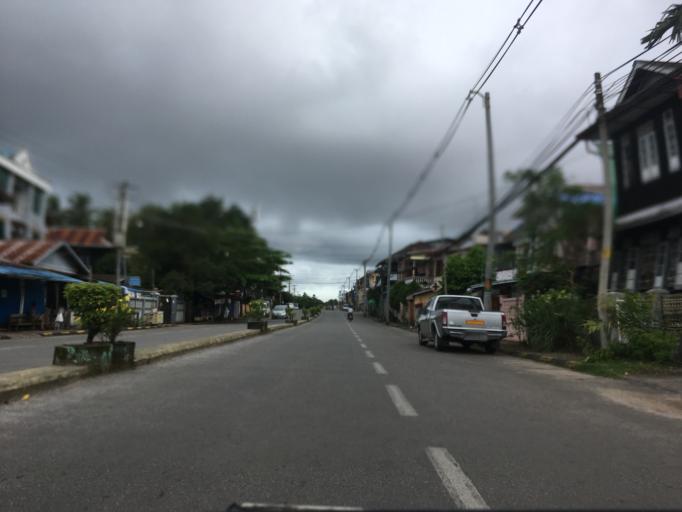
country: MM
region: Mon
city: Mawlamyine
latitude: 16.4755
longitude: 97.6223
